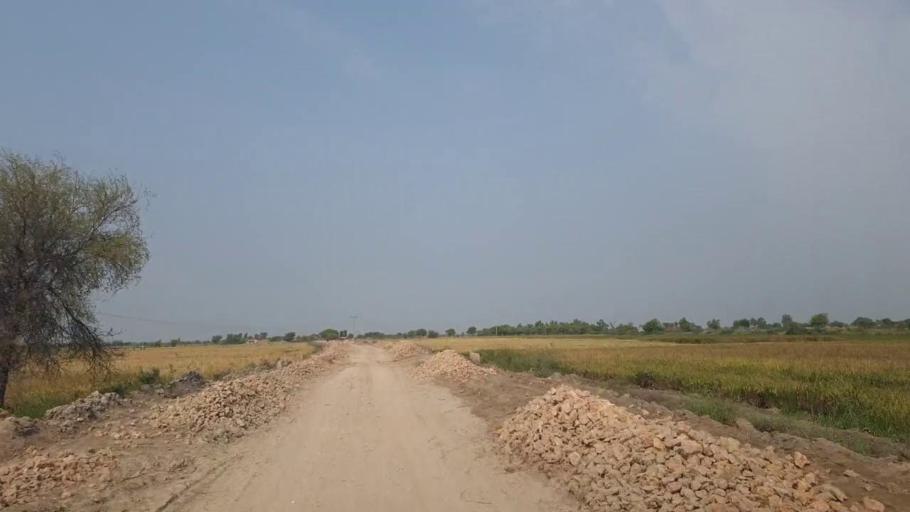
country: PK
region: Sindh
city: Badin
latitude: 24.6111
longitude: 68.7415
